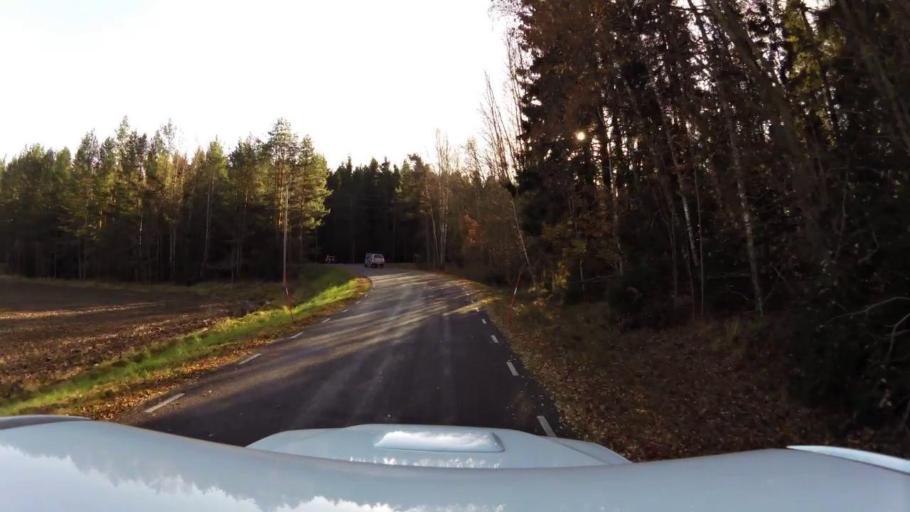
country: SE
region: OEstergoetland
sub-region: Linkopings Kommun
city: Linghem
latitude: 58.4597
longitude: 15.7757
